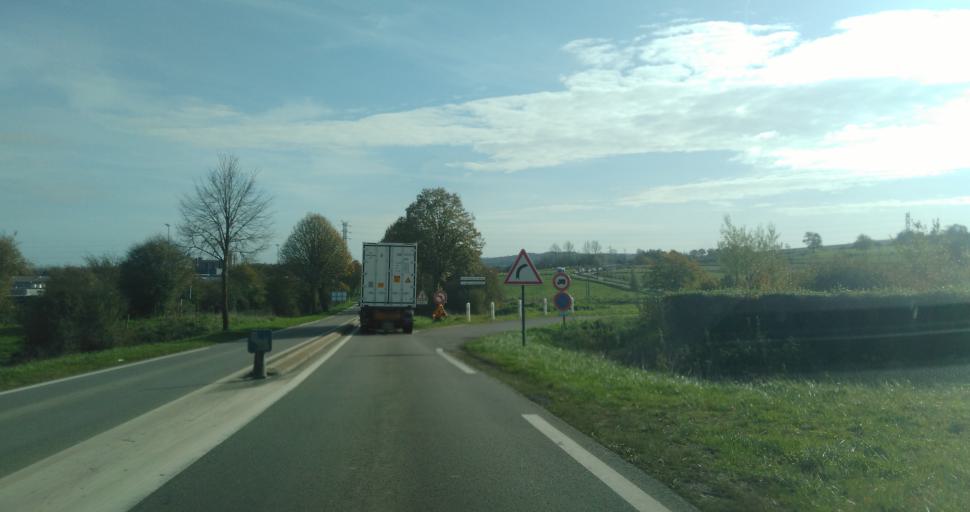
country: FR
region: Nord-Pas-de-Calais
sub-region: Departement du Pas-de-Calais
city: Hesdin
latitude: 50.3674
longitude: 2.0307
